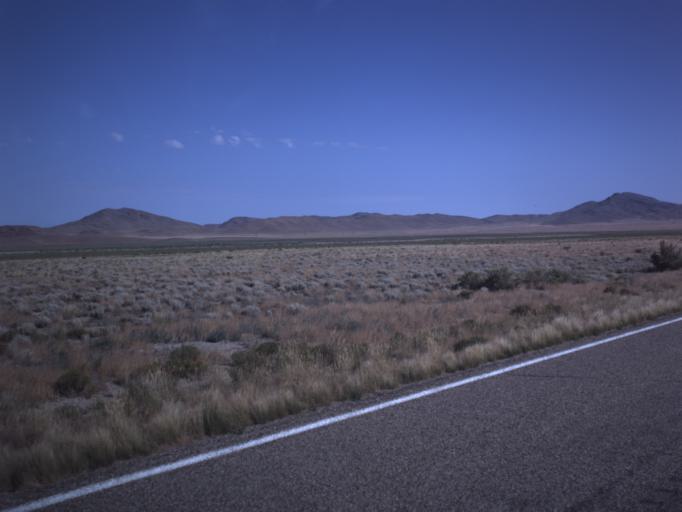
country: US
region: Utah
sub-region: Beaver County
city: Milford
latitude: 38.6694
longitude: -112.9807
